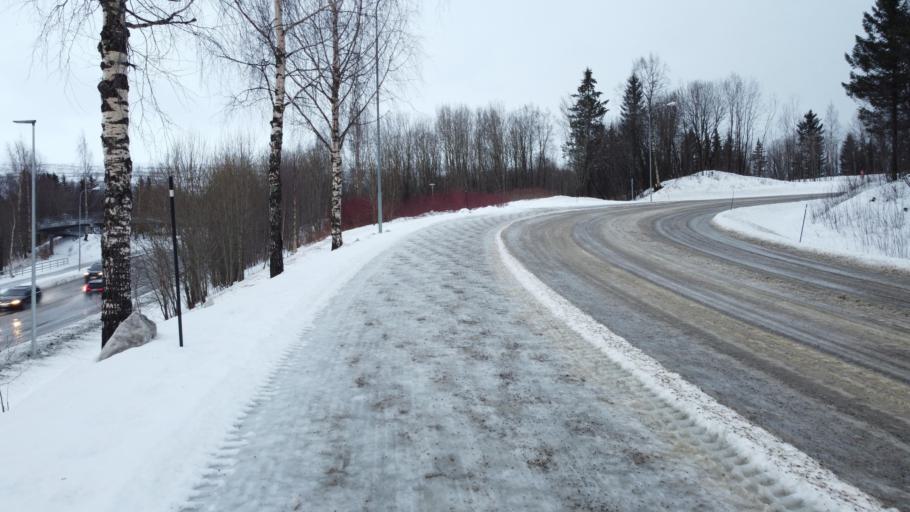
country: NO
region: Nordland
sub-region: Rana
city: Mo i Rana
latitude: 66.3274
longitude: 14.1584
